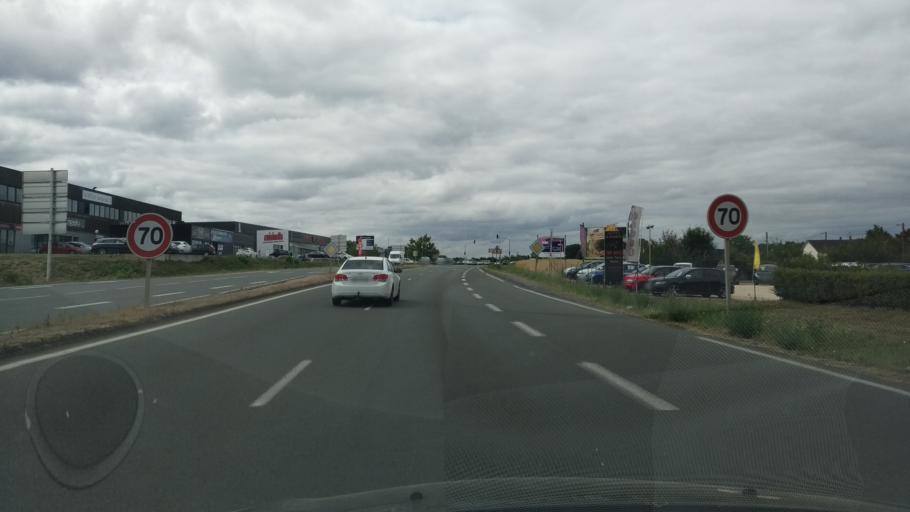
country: FR
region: Poitou-Charentes
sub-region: Departement de la Vienne
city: Biard
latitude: 46.5551
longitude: 0.3062
